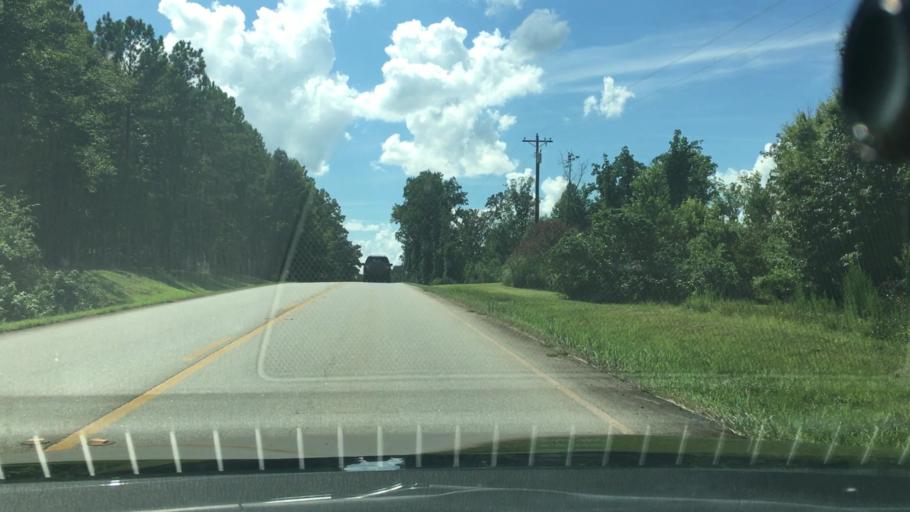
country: US
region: Georgia
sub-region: Jasper County
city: Monticello
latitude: 33.3054
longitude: -83.6006
